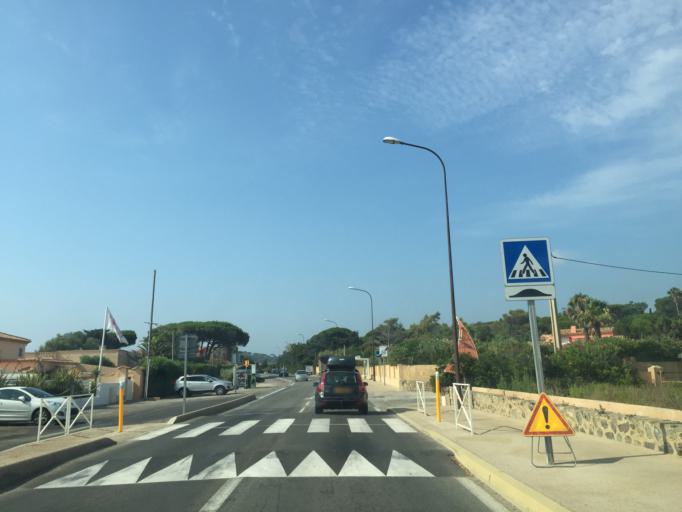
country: FR
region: Provence-Alpes-Cote d'Azur
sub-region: Departement du Var
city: Sainte-Maxime
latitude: 43.3296
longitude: 6.6677
